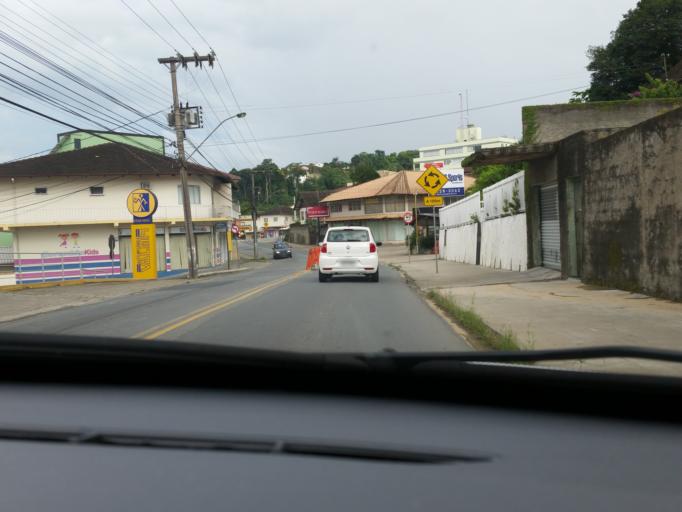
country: BR
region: Santa Catarina
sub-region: Blumenau
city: Blumenau
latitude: -26.9117
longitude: -49.1023
